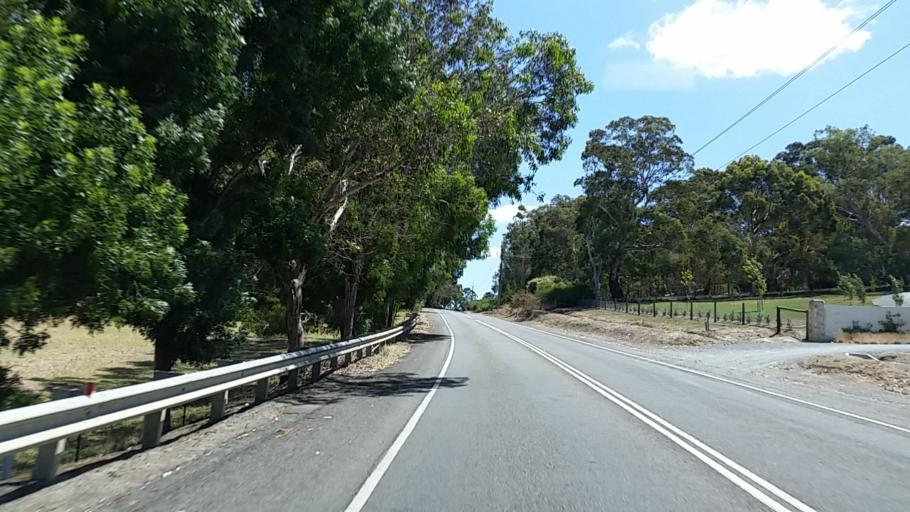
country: AU
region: South Australia
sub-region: Mount Barker
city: Nairne
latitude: -35.0399
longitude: 138.8894
